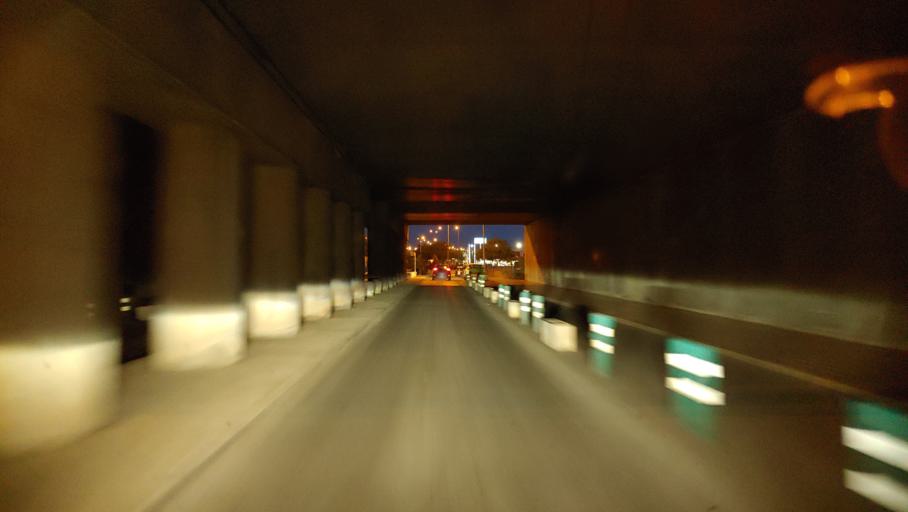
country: ES
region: Castille-La Mancha
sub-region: Provincia de Ciudad Real
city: Ciudad Real
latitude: 38.9844
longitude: -3.9128
